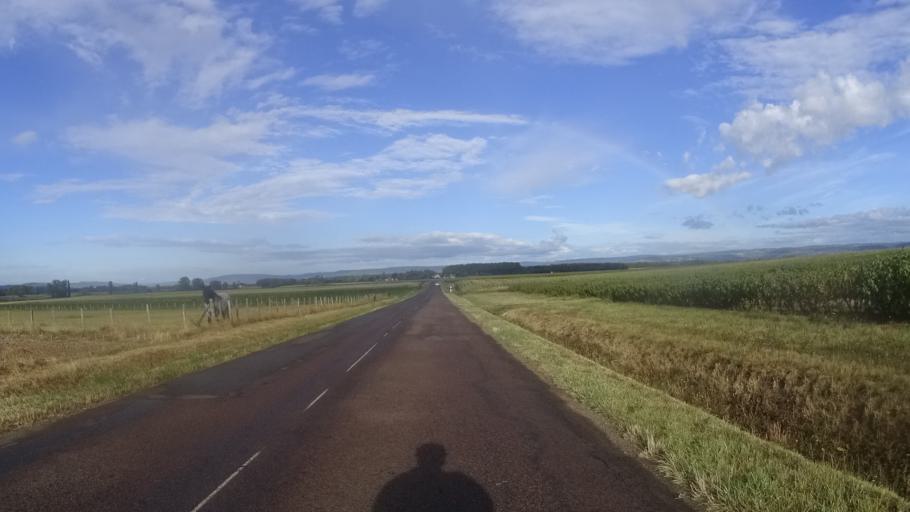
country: FR
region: Bourgogne
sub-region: Departement de Saone-et-Loire
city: Demigny
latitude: 46.9579
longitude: 4.8831
